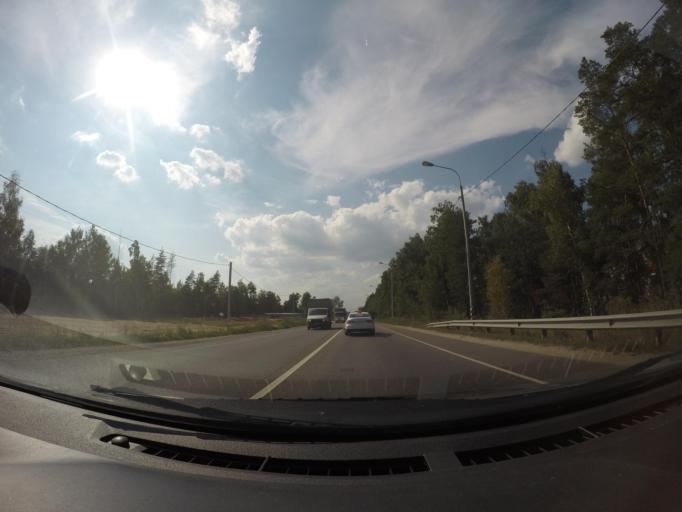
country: RU
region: Moskovskaya
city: Il'inskiy
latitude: 55.6524
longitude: 38.1229
